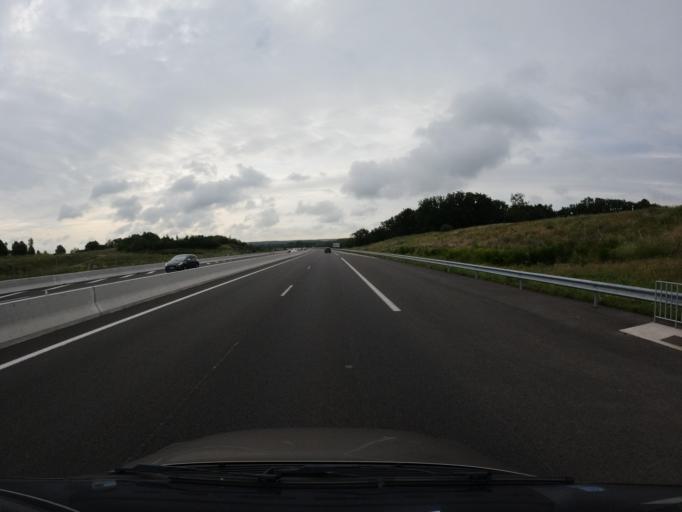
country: FR
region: Centre
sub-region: Departement d'Indre-et-Loire
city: Langeais
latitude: 47.3386
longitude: 0.4285
